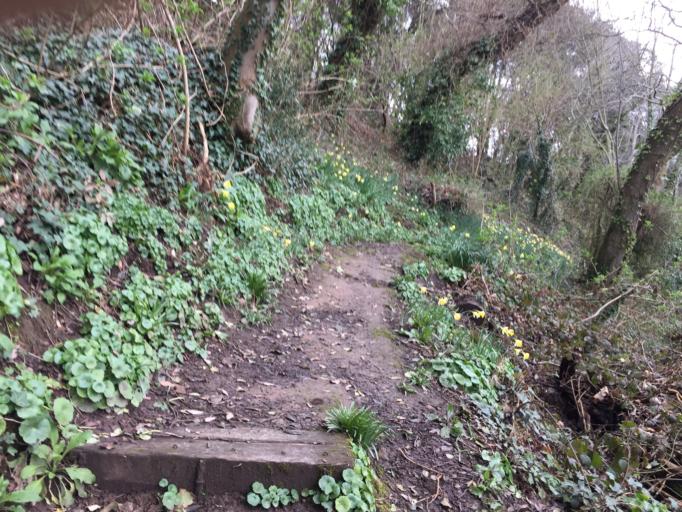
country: JE
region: St Helier
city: Saint Helier
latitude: 49.2175
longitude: -2.1347
